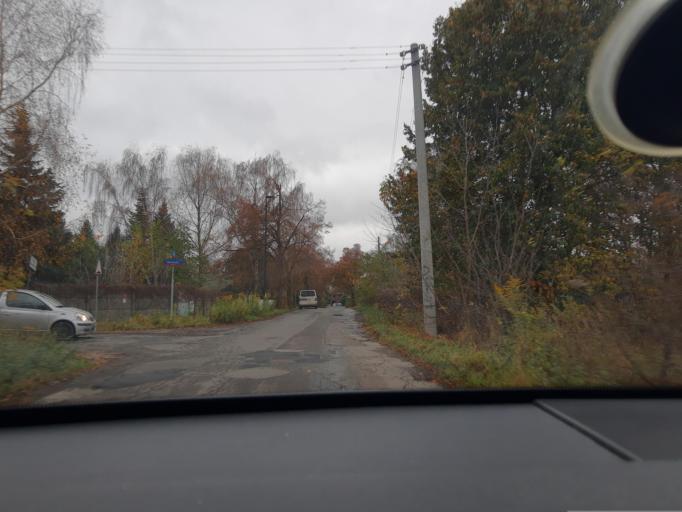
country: PL
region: Lodz Voivodeship
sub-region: Powiat pabianicki
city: Konstantynow Lodzki
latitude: 51.7450
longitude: 19.3714
